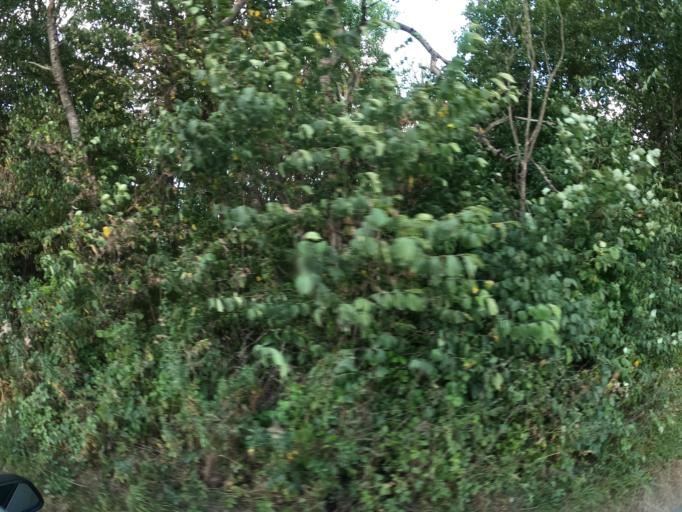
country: SE
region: Skane
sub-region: Lunds Kommun
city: Lund
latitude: 55.7106
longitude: 13.3194
